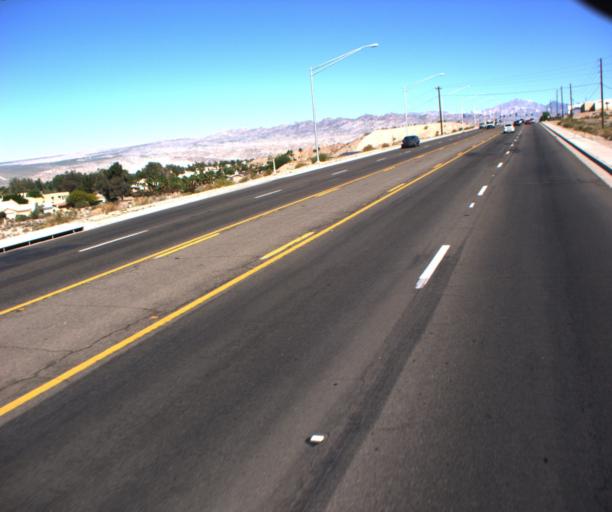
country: US
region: Arizona
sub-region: Mohave County
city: Bullhead City
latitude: 35.0775
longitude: -114.5938
